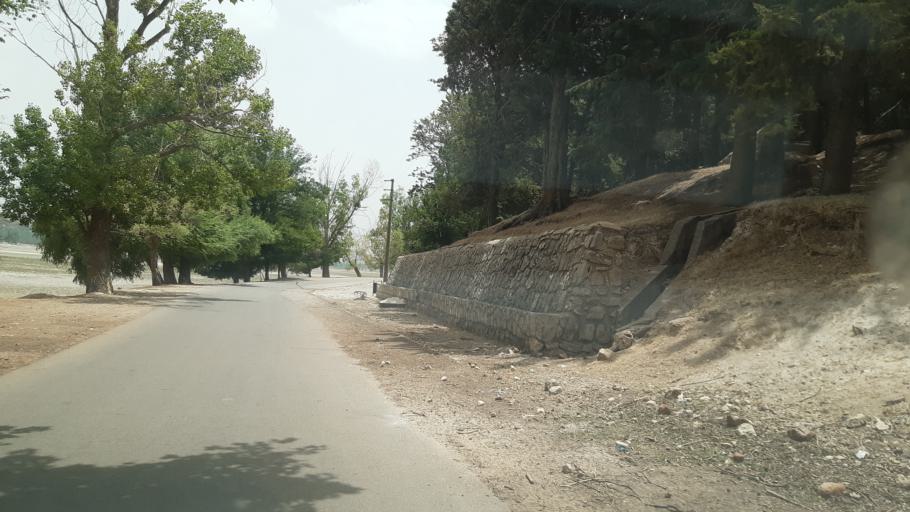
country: MA
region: Meknes-Tafilalet
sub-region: Ifrane
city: Ifrane
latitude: 33.6525
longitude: -5.0424
